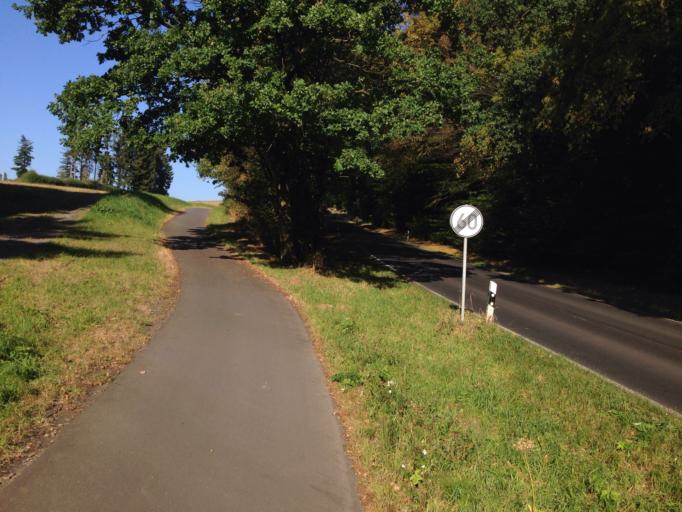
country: DE
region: Hesse
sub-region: Regierungsbezirk Giessen
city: Giessen
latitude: 50.6322
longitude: 8.6505
